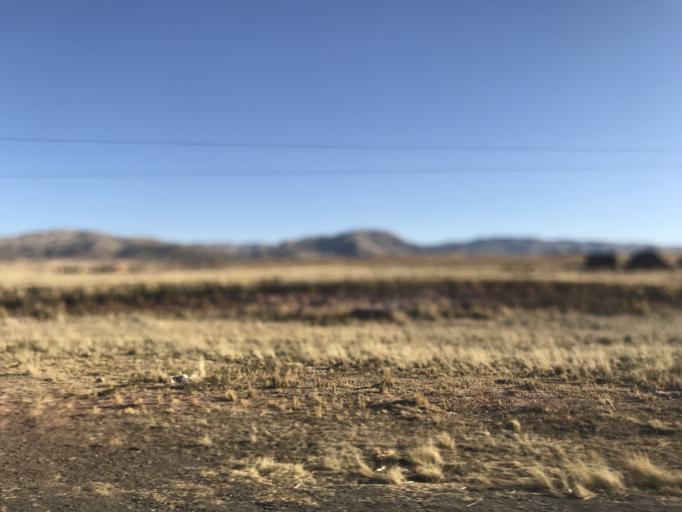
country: BO
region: La Paz
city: Tiahuanaco
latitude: -16.5643
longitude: -68.6213
